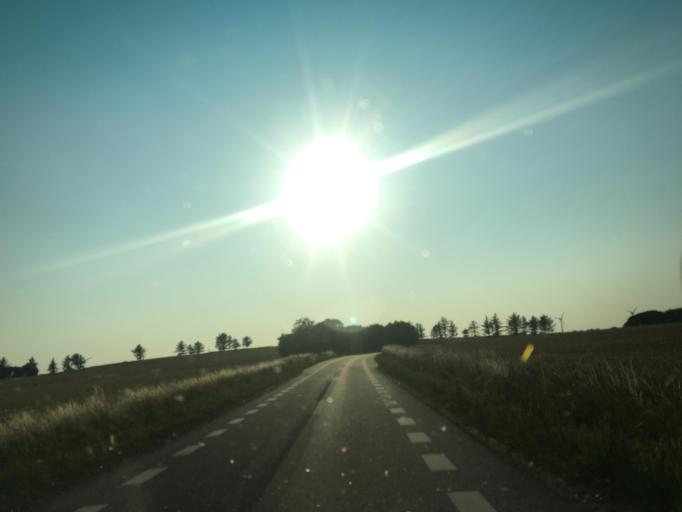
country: DK
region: North Denmark
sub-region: Thisted Kommune
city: Hurup
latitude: 56.8169
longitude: 8.3715
